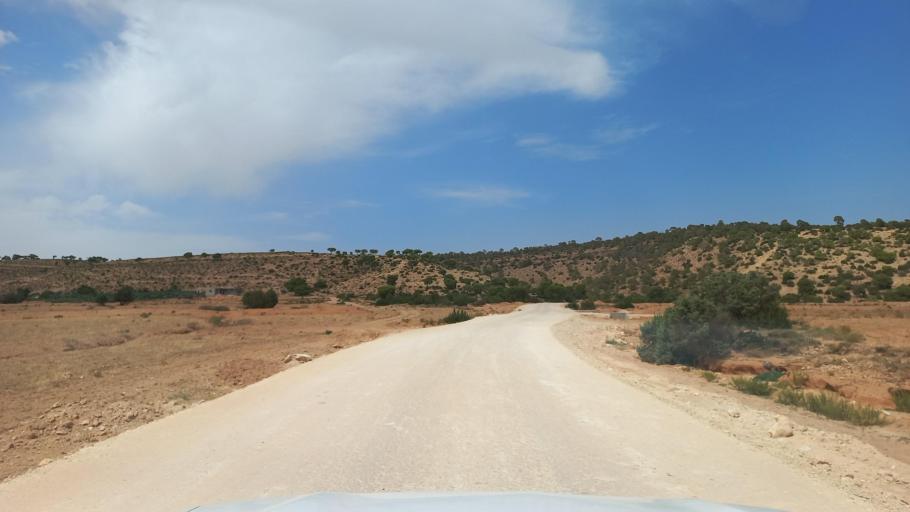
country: TN
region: Al Qasrayn
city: Kasserine
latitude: 35.3714
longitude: 8.8883
